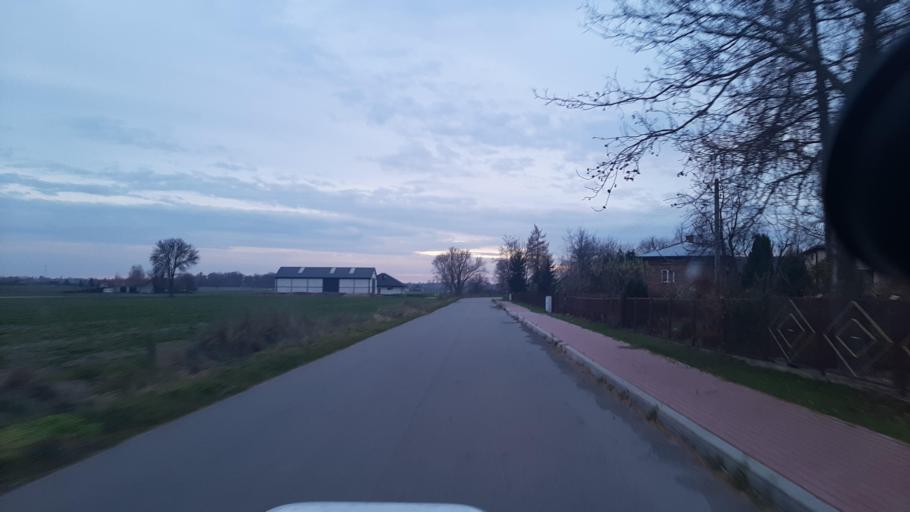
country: PL
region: Lublin Voivodeship
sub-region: Powiat lubelski
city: Garbow
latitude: 51.3670
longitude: 22.3844
